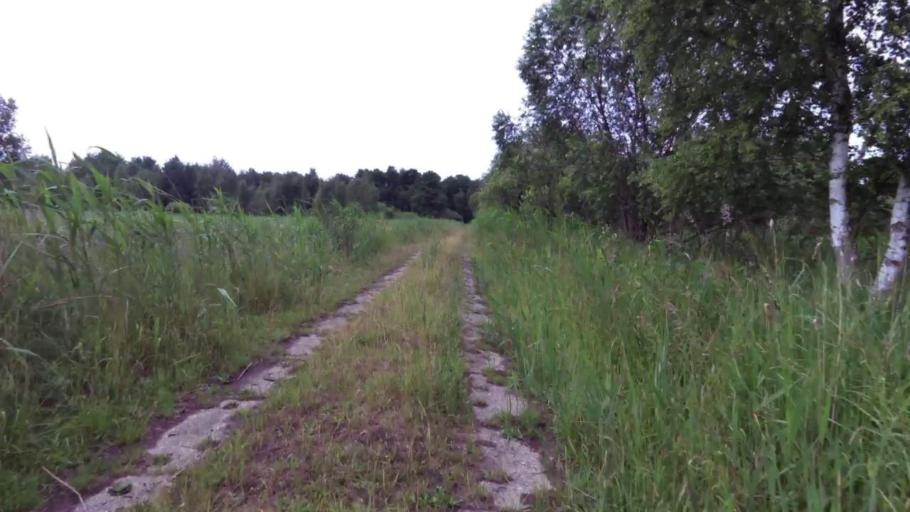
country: PL
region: West Pomeranian Voivodeship
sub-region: Powiat goleniowski
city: Stepnica
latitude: 53.7380
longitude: 14.6033
